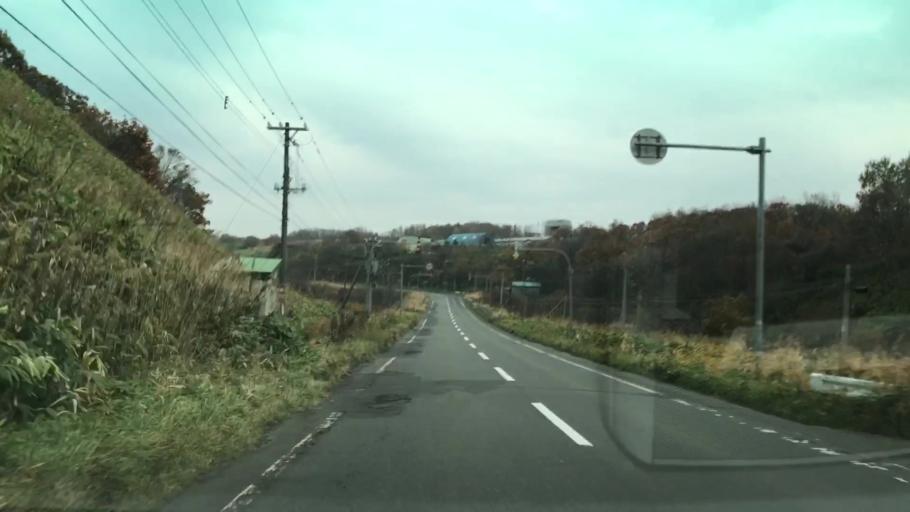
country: JP
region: Hokkaido
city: Ishikari
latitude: 43.3357
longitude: 141.4277
